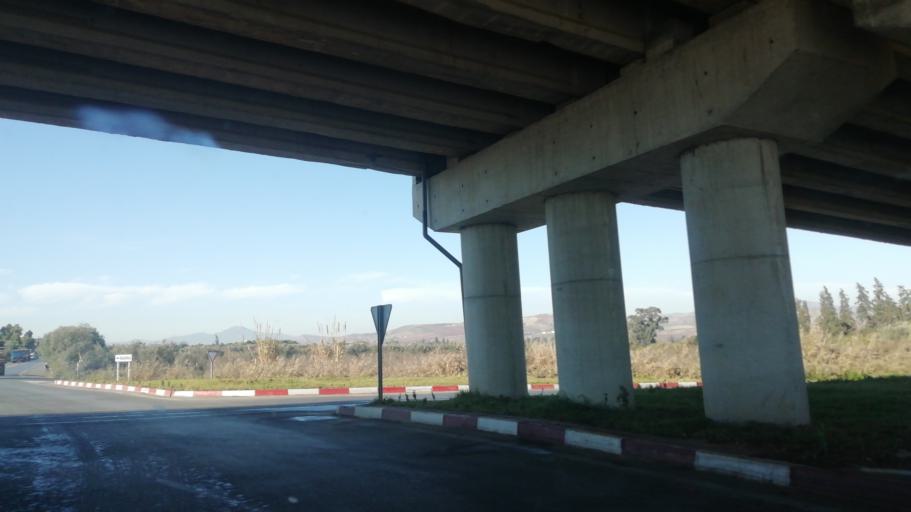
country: DZ
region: Tlemcen
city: Remchi
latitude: 35.0848
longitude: -1.4369
